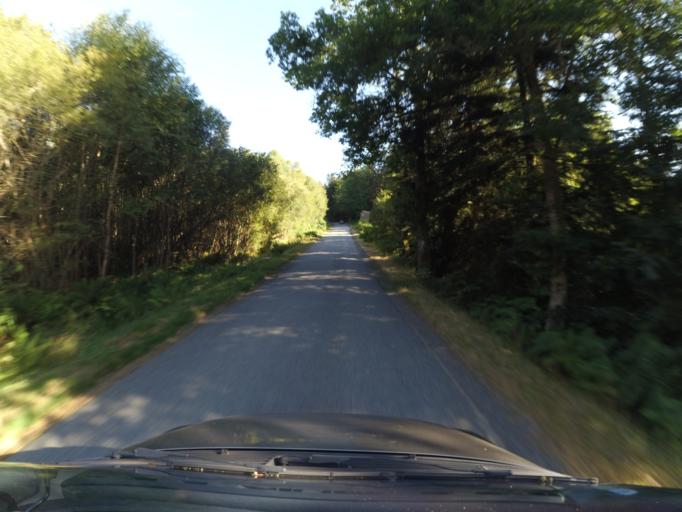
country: FR
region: Limousin
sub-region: Departement de la Creuse
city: Banize
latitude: 45.7828
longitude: 1.9741
